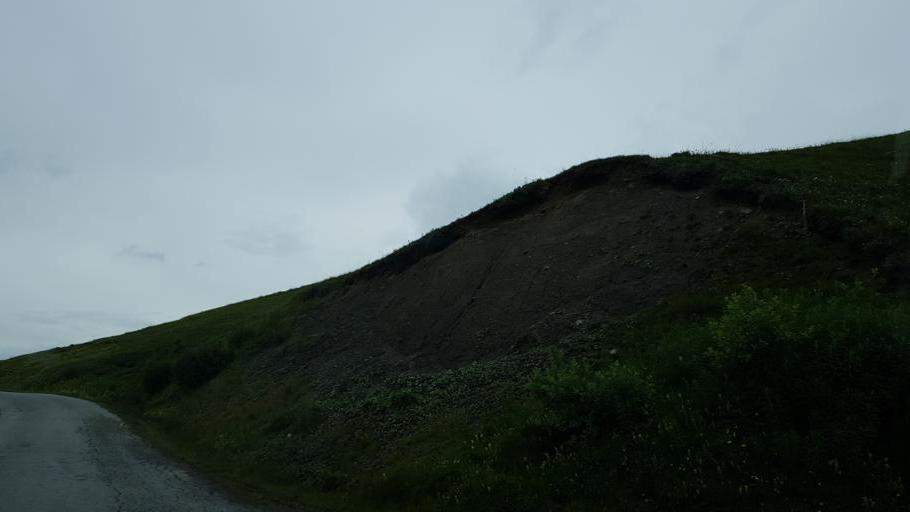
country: IT
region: Piedmont
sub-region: Provincia di Cuneo
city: Serre
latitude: 44.5431
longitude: 7.1194
